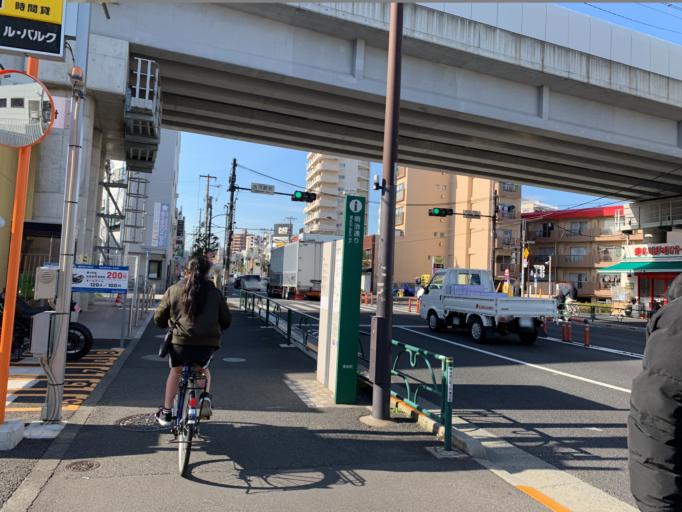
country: JP
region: Tokyo
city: Urayasu
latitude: 35.7192
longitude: 139.8213
